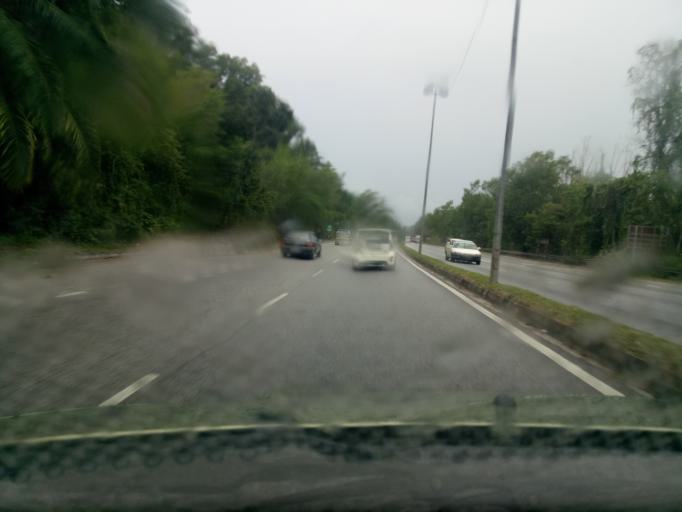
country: MY
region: Kedah
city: Sungai Petani
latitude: 5.6469
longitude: 100.5389
